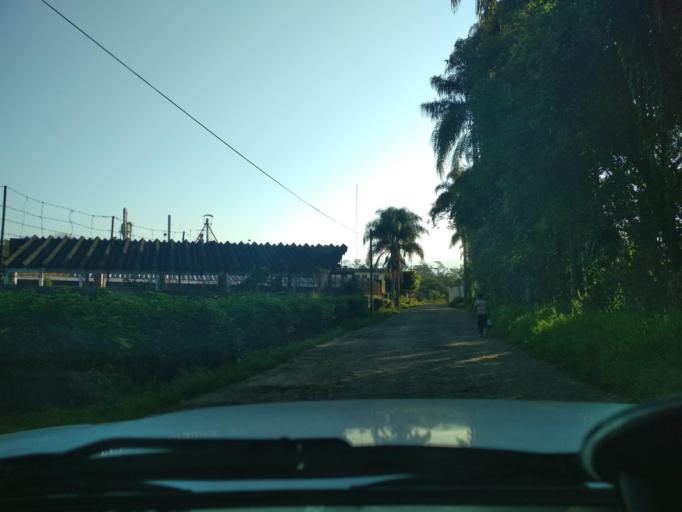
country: MX
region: Veracruz
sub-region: Fortin
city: Fraccionamiento Villas de la Llave
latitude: 18.9245
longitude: -96.9925
